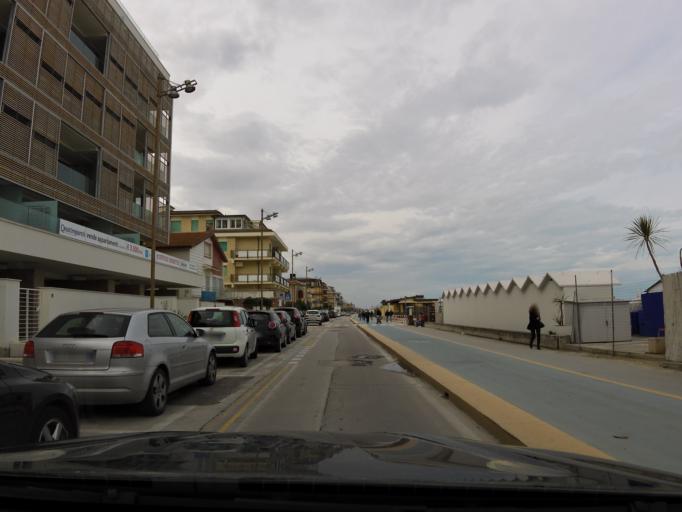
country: IT
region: The Marches
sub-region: Provincia di Macerata
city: Civitanova Marche
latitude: 43.3213
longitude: 13.7197
